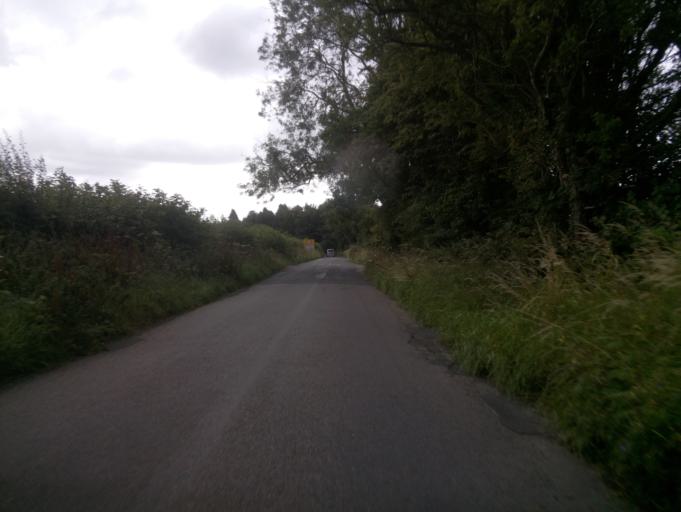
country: GB
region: England
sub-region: Gloucestershire
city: Shurdington
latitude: 51.7953
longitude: -2.1218
